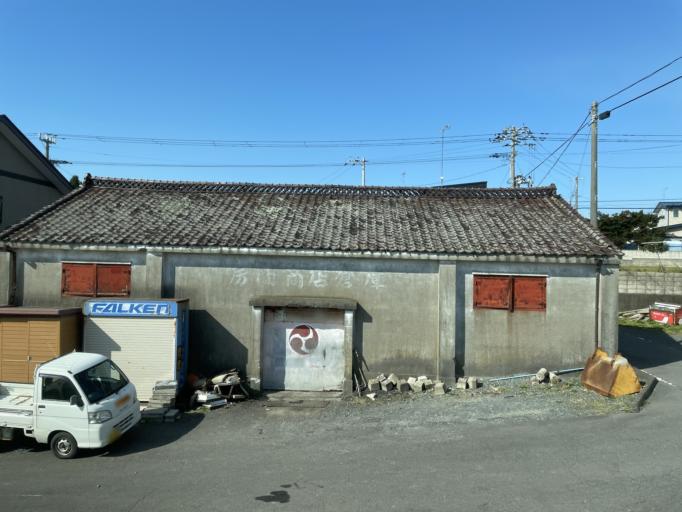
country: JP
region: Aomori
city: Hachinohe
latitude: 40.4583
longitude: 141.6633
